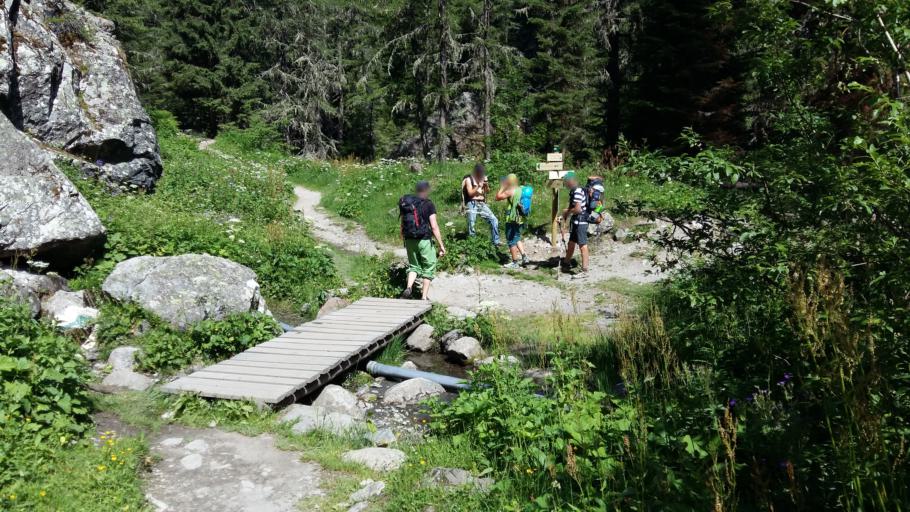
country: FR
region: Rhone-Alpes
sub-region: Departement de la Haute-Savoie
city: Chamonix-Mont-Blanc
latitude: 46.0182
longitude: 6.9031
